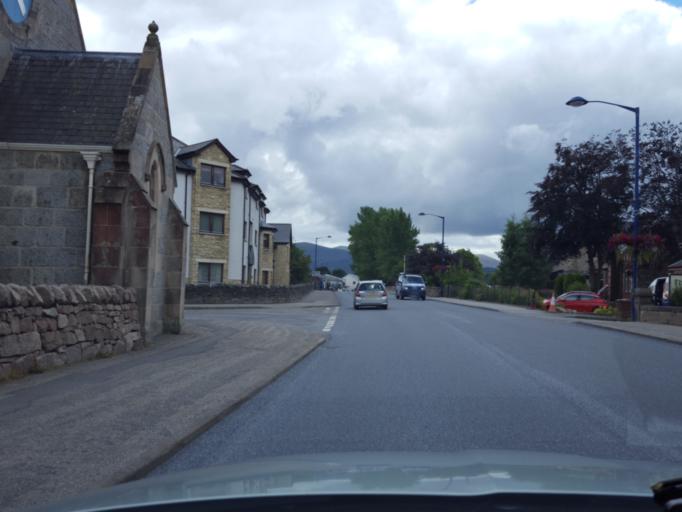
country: GB
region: Scotland
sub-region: Highland
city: Aviemore
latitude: 57.1945
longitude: -3.8291
